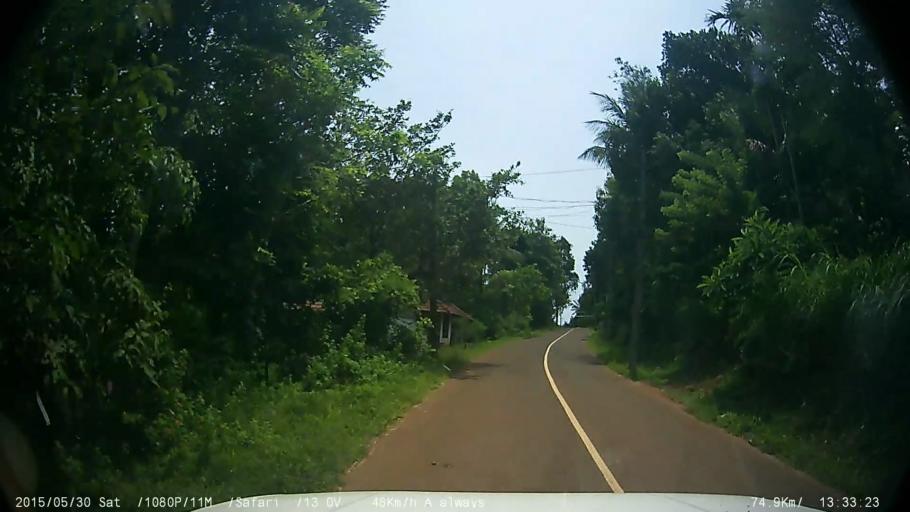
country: IN
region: Kerala
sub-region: Wayanad
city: Panamaram
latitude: 11.8200
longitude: 76.0726
